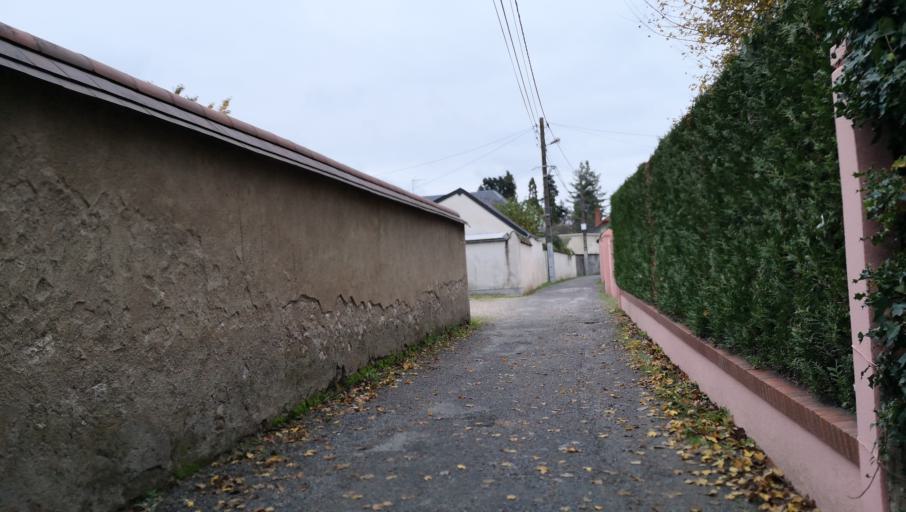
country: FR
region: Centre
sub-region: Departement du Loiret
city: Saint-Jean-le-Blanc
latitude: 47.9029
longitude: 1.9364
